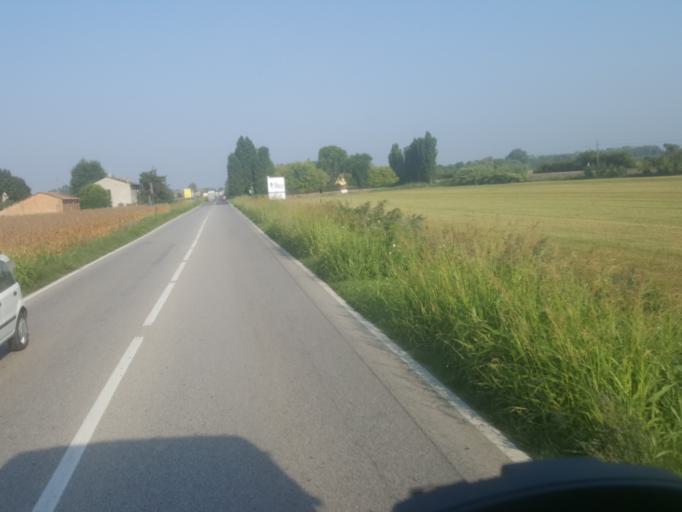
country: IT
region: Emilia-Romagna
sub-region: Provincia di Ravenna
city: Mezzano
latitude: 44.4504
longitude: 12.1185
